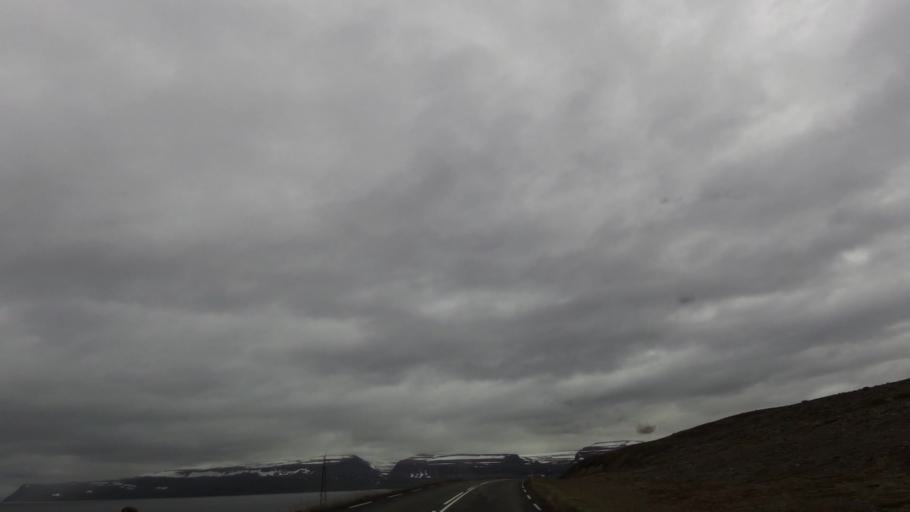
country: IS
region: Westfjords
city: Isafjoerdur
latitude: 66.0471
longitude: -22.7702
